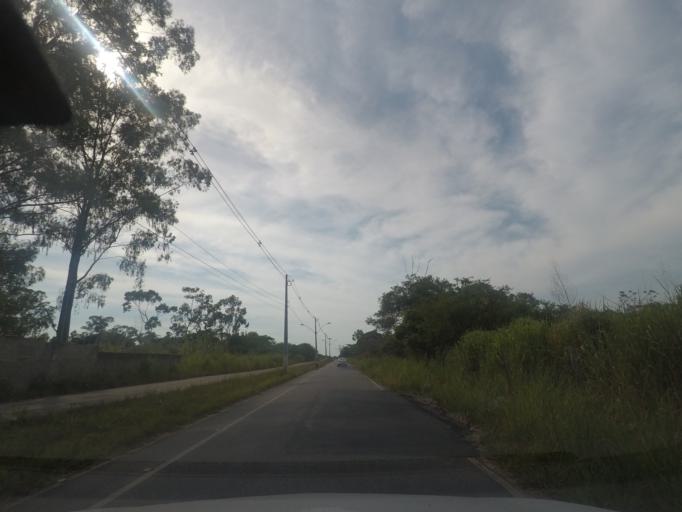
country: BR
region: Rio de Janeiro
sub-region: Marica
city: Marica
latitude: -22.9437
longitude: -42.8920
